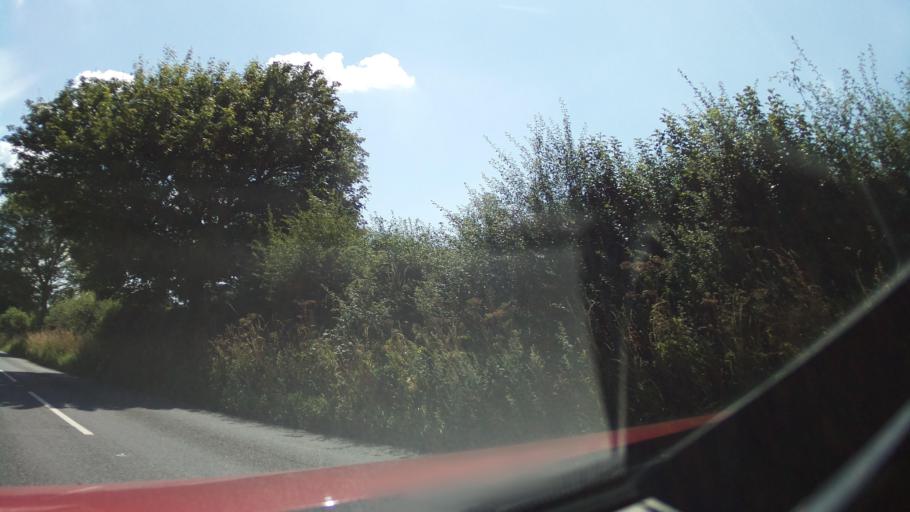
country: GB
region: England
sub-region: West Berkshire
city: Winterbourne
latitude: 51.4831
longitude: -1.3614
